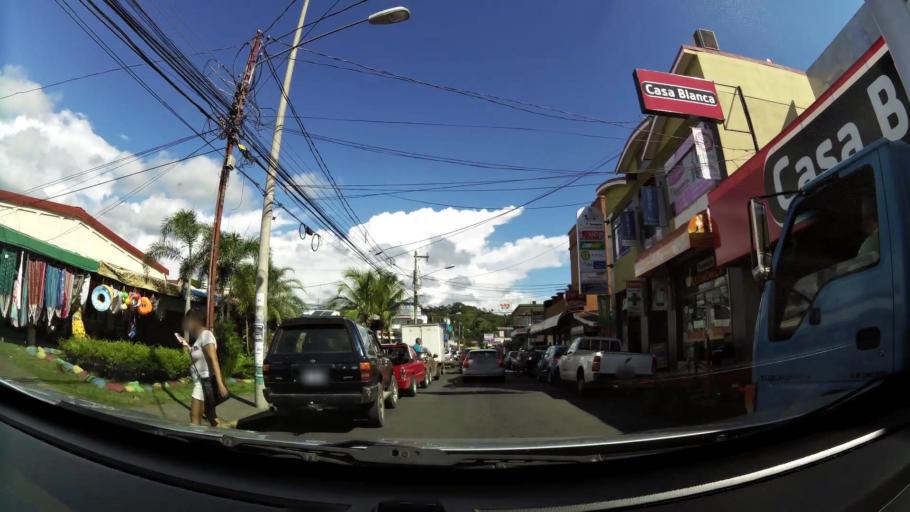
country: CR
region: Puntarenas
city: Quepos
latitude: 9.4303
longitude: -84.1633
